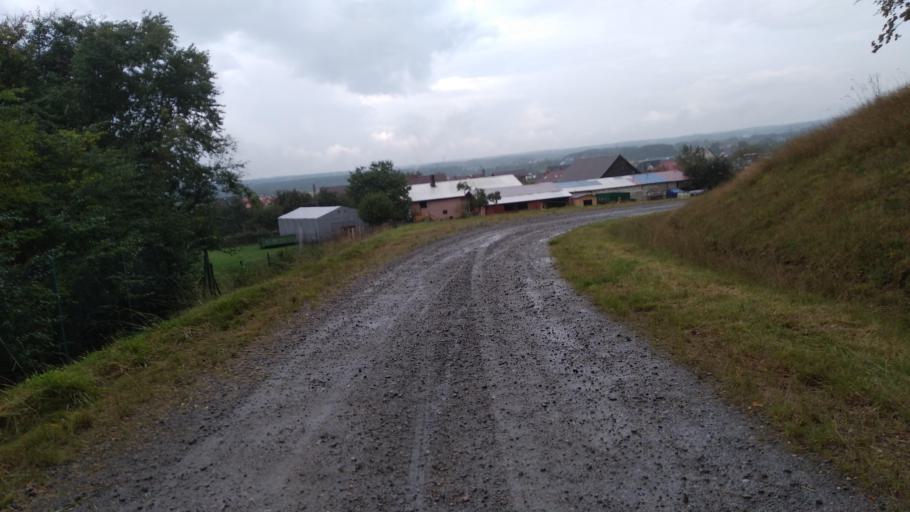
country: PL
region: Pomeranian Voivodeship
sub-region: Powiat wejherowski
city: Goscicino
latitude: 54.6328
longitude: 18.1350
